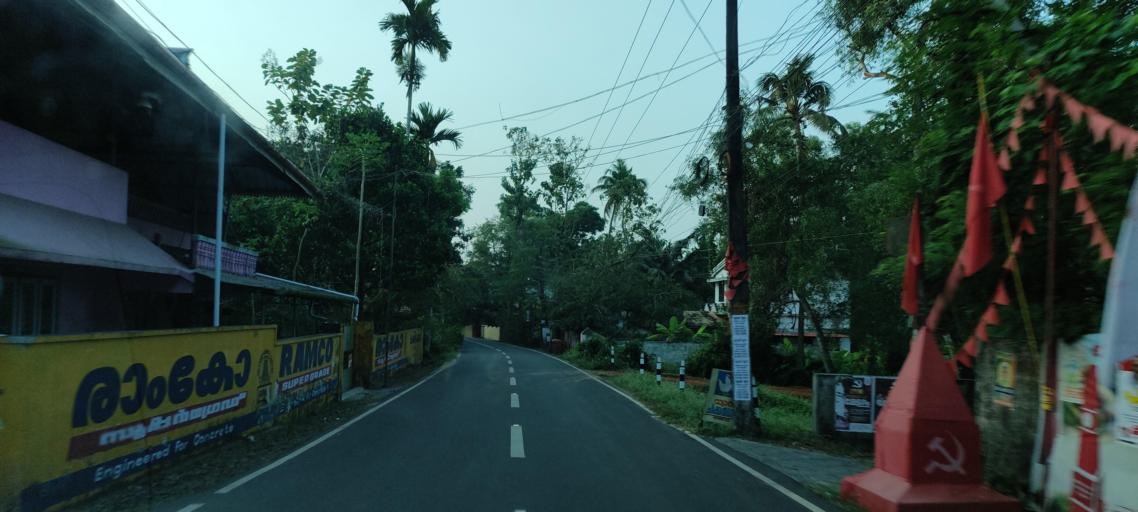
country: IN
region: Kerala
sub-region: Alappuzha
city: Alleppey
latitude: 9.4460
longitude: 76.3460
